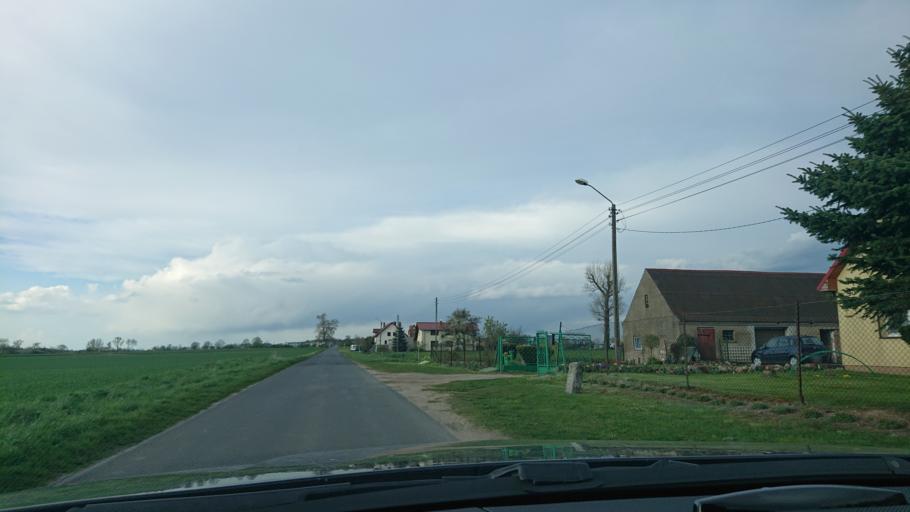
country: PL
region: Greater Poland Voivodeship
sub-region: Powiat gnieznienski
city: Klecko
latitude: 52.5812
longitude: 17.4816
